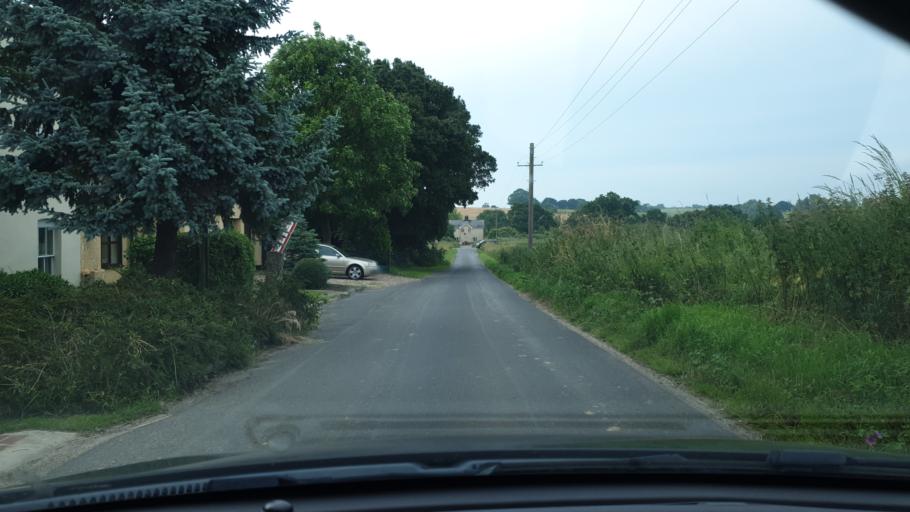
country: GB
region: England
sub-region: Suffolk
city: Shotley Gate
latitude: 51.9227
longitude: 1.1998
